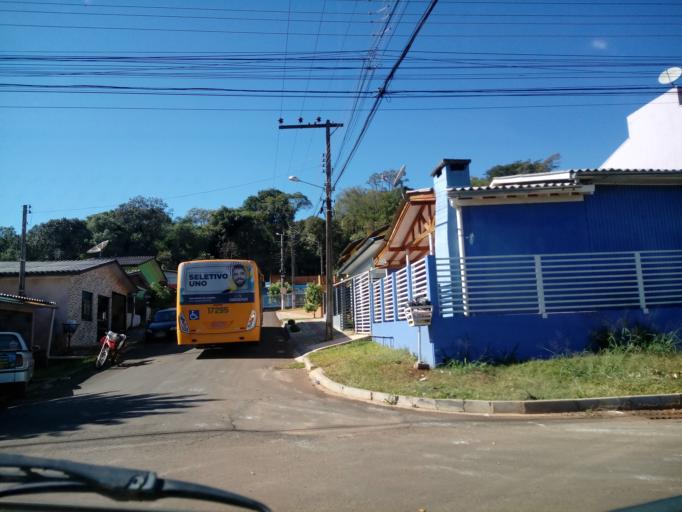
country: BR
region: Santa Catarina
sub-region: Chapeco
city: Chapeco
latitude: -27.0923
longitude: -52.6820
